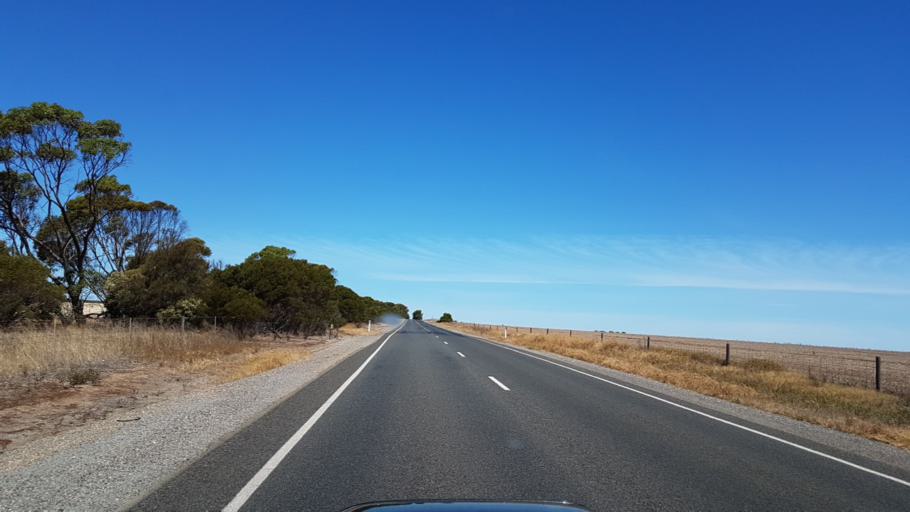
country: AU
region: South Australia
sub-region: Yorke Peninsula
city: Maitland
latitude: -34.3430
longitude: 137.6589
